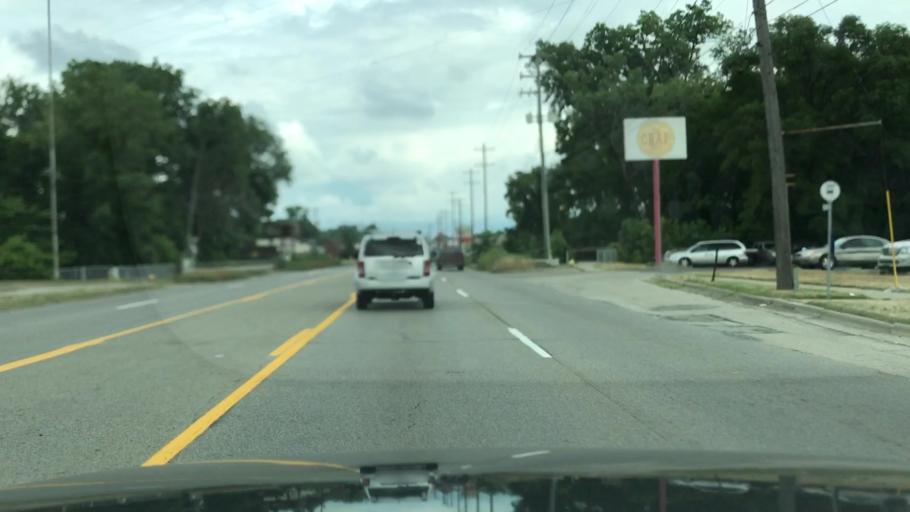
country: US
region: Michigan
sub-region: Kent County
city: Kentwood
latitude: 42.9128
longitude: -85.6518
